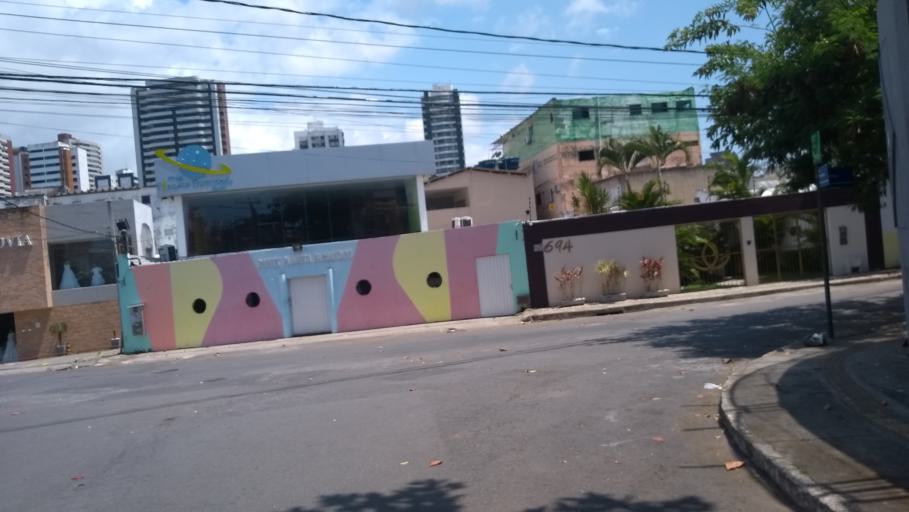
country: BR
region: Bahia
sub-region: Salvador
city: Salvador
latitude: -12.9907
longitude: -38.4592
